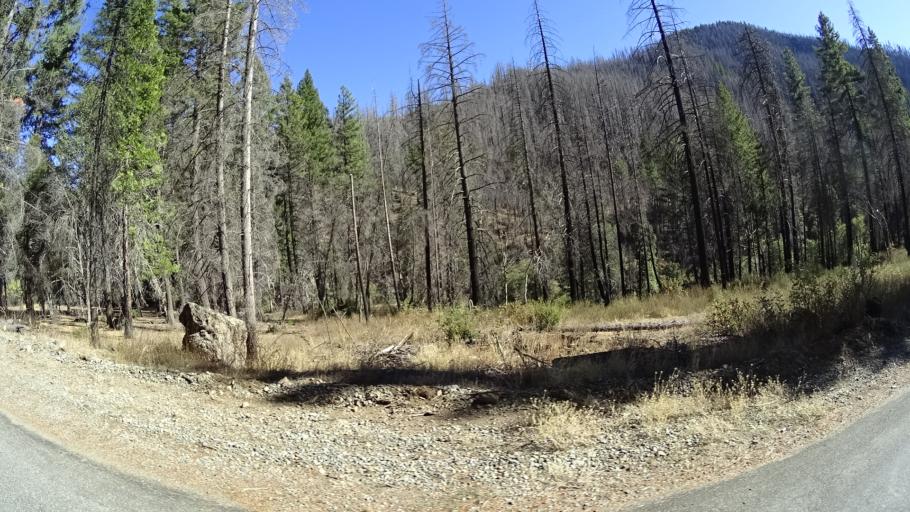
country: US
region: California
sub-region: Siskiyou County
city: Happy Camp
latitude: 41.3024
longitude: -123.0759
